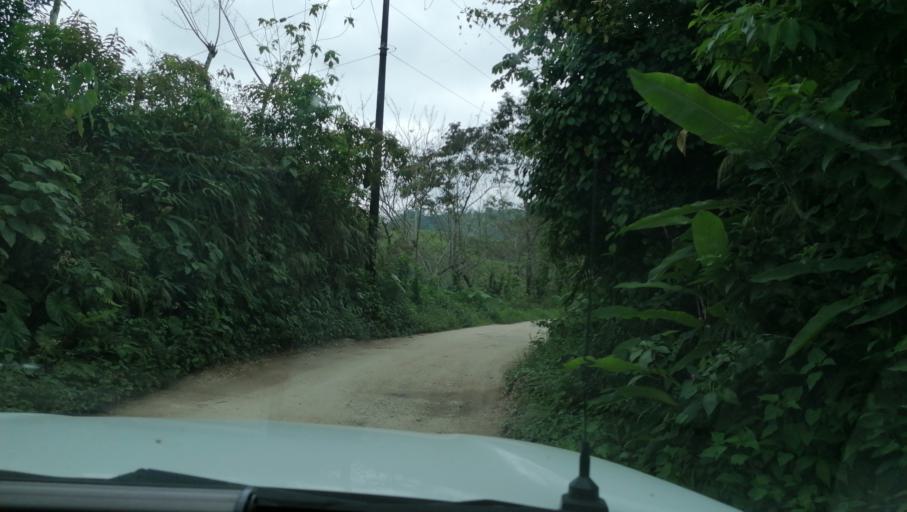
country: MX
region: Chiapas
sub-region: Ocotepec
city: San Pablo Huacano
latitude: 17.2741
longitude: -93.2362
